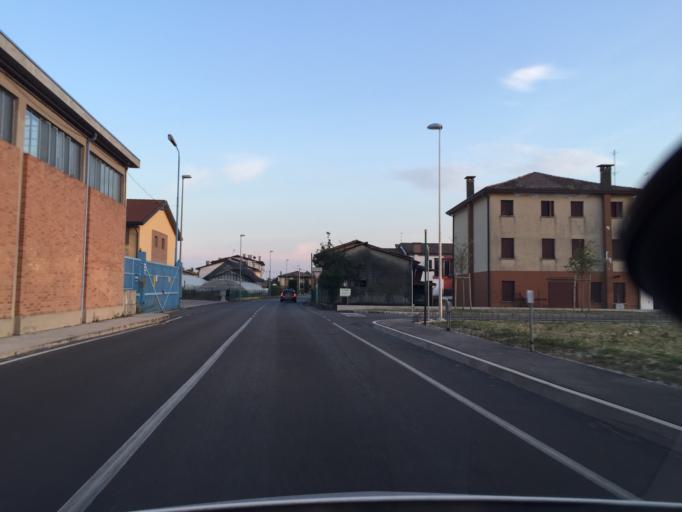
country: IT
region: Veneto
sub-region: Provincia di Padova
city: Cittadella
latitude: 45.6423
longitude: 11.7833
